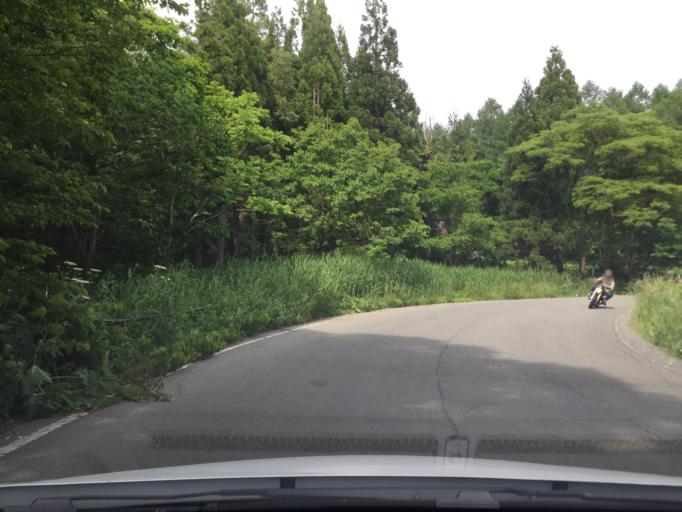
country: JP
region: Fukushima
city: Inawashiro
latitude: 37.7290
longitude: 140.0576
